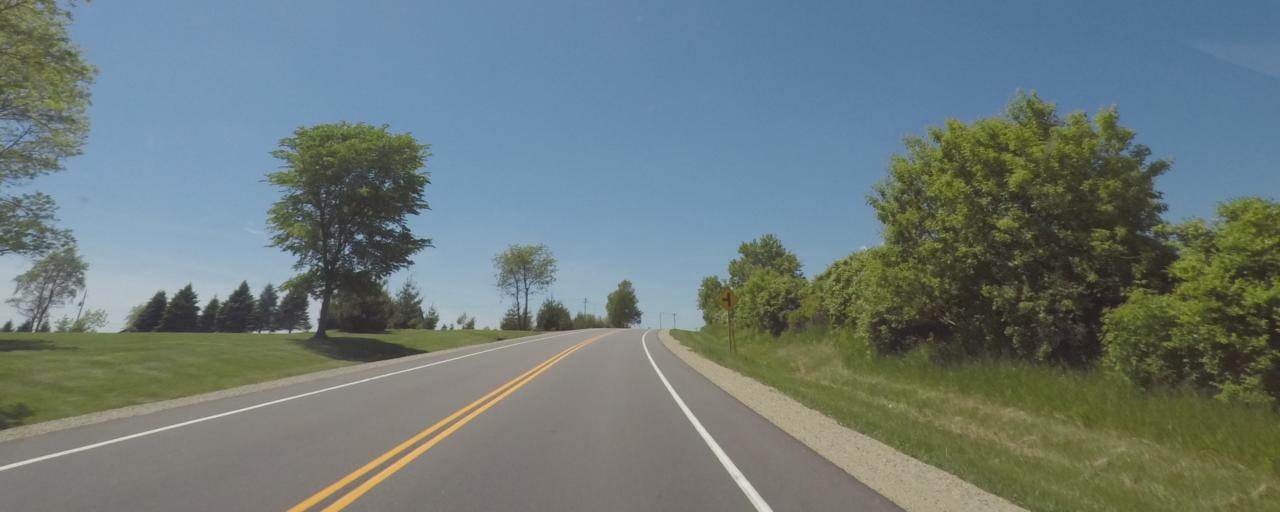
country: US
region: Wisconsin
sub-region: Dane County
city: Fitchburg
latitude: 42.9510
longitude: -89.4588
